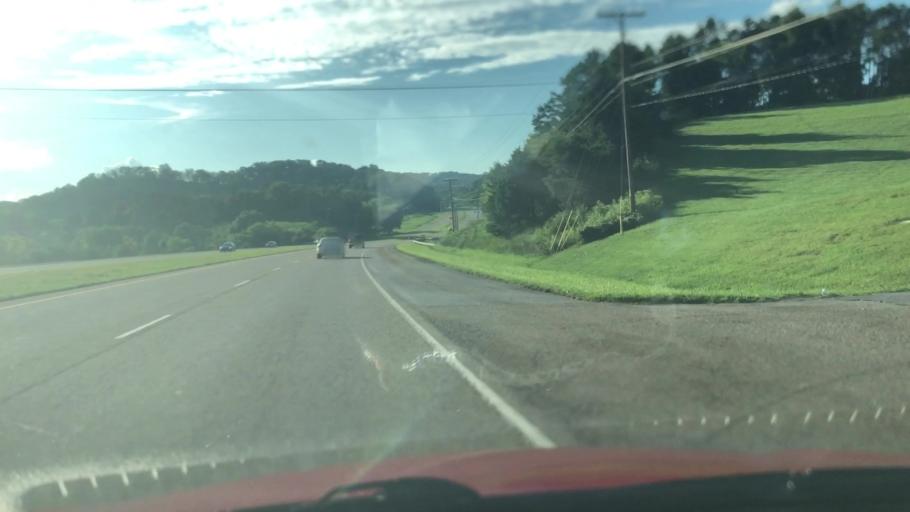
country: US
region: Tennessee
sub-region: Jefferson County
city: Dandridge
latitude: 36.0481
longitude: -83.4601
